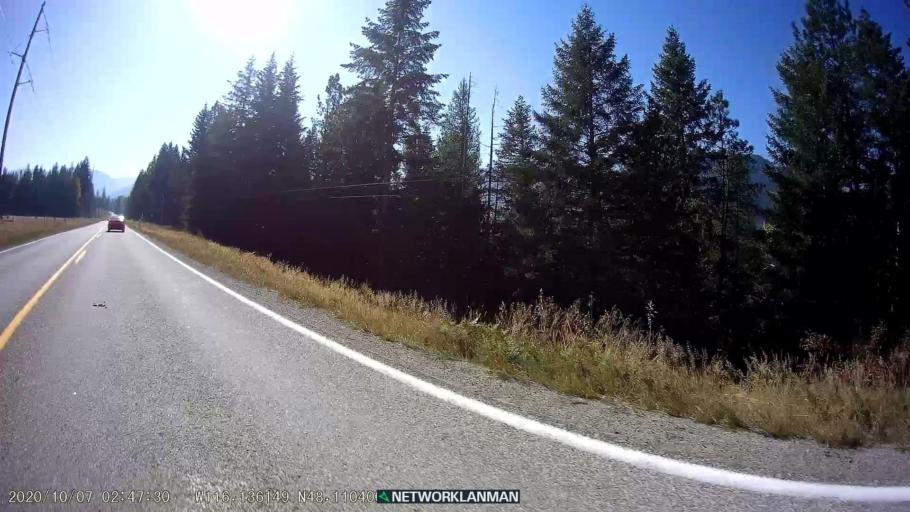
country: US
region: Idaho
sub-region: Bonner County
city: Ponderay
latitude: 48.1102
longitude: -116.1361
